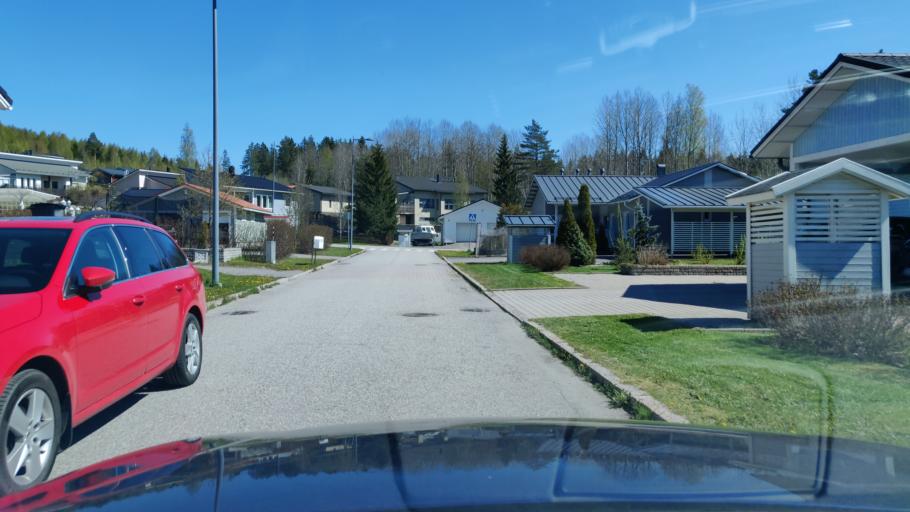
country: FI
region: Uusimaa
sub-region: Helsinki
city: Nurmijaervi
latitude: 60.3613
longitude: 24.7550
